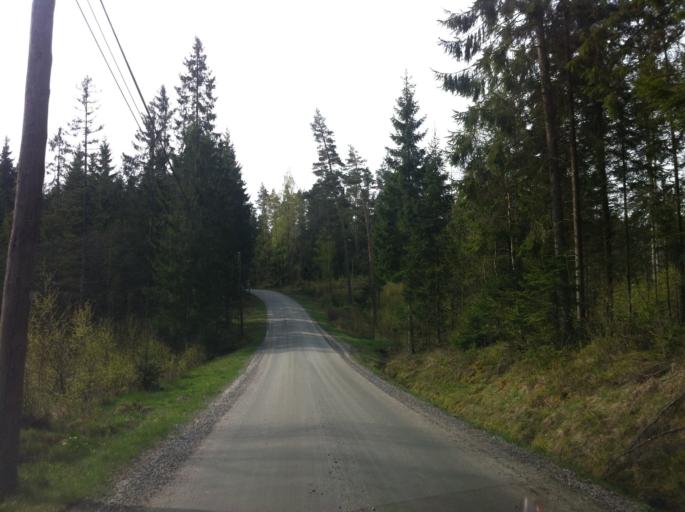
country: SE
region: Vaestra Goetaland
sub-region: Bollebygds Kommun
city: Bollebygd
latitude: 57.7584
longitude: 12.5915
